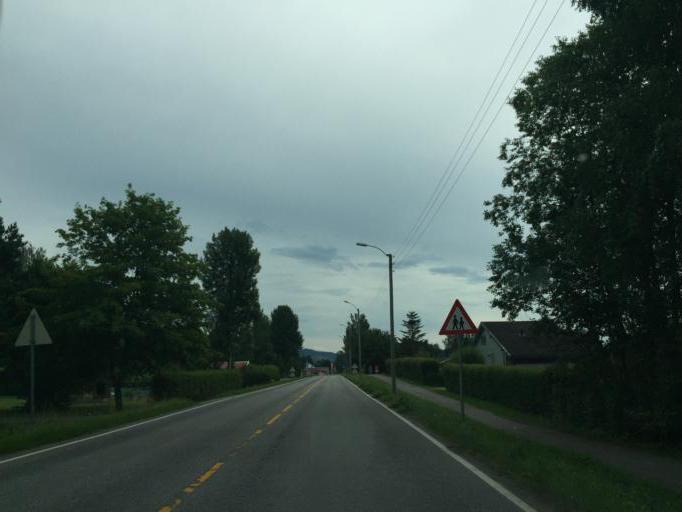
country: NO
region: Hedmark
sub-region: Kongsvinger
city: Kongsvinger
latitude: 60.1984
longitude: 11.9946
